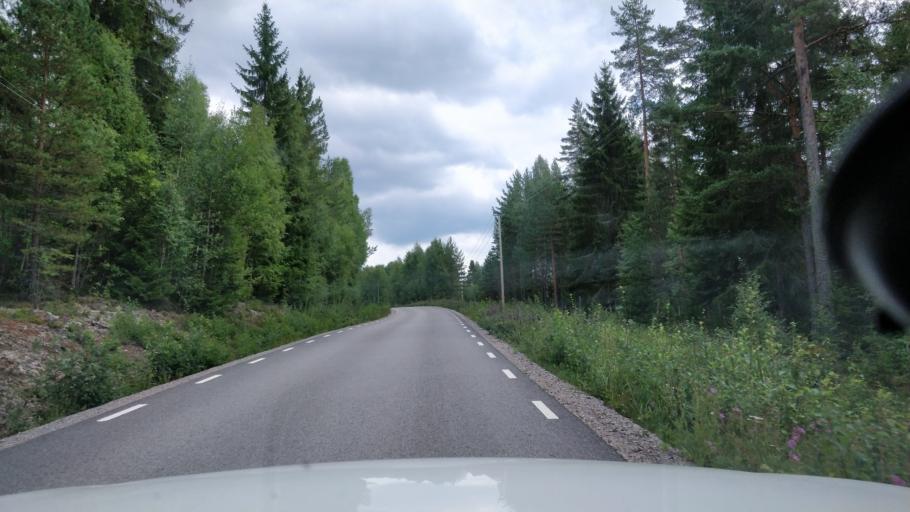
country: SE
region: Dalarna
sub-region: Faluns Kommun
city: Bjursas
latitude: 60.7516
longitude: 15.4966
